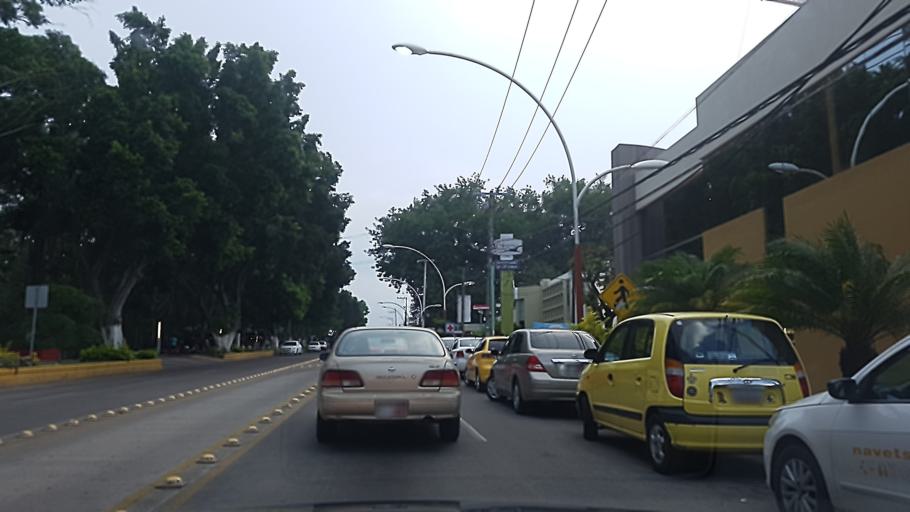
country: MX
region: Nayarit
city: Tepic
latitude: 21.5056
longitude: -104.9016
